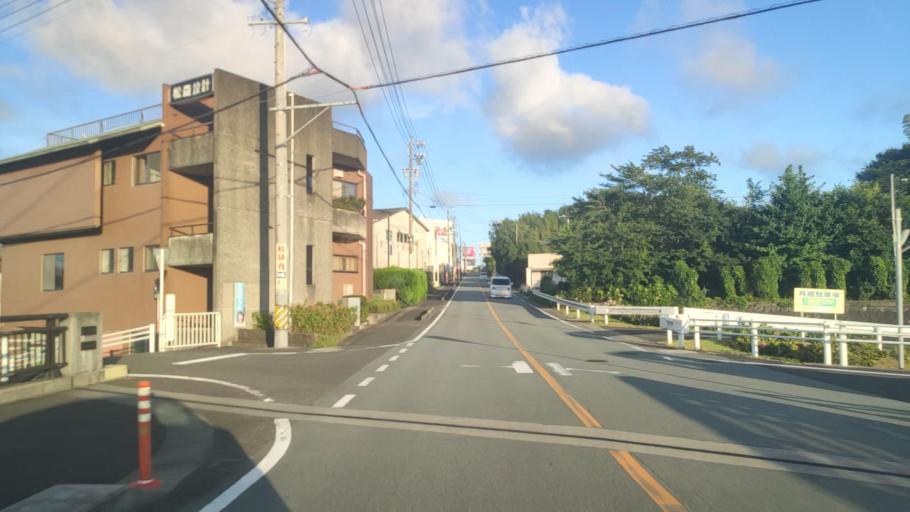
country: JP
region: Mie
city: Toba
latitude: 34.3274
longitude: 136.8238
